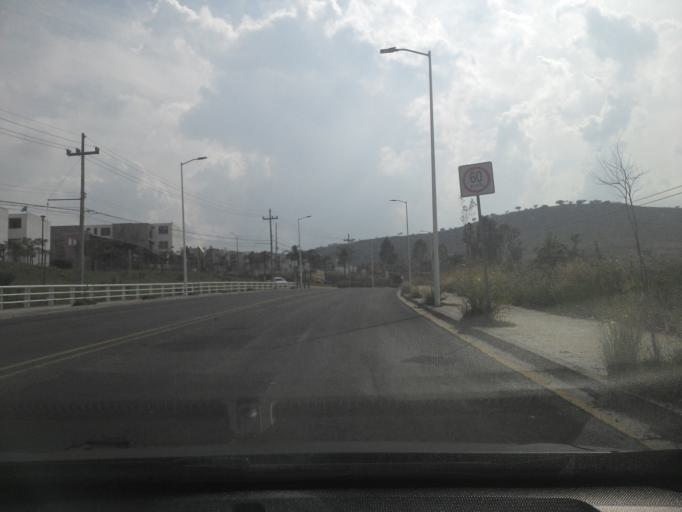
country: MX
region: Jalisco
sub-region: Tlajomulco de Zuniga
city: Lomas del Sur
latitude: 20.4921
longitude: -103.4179
